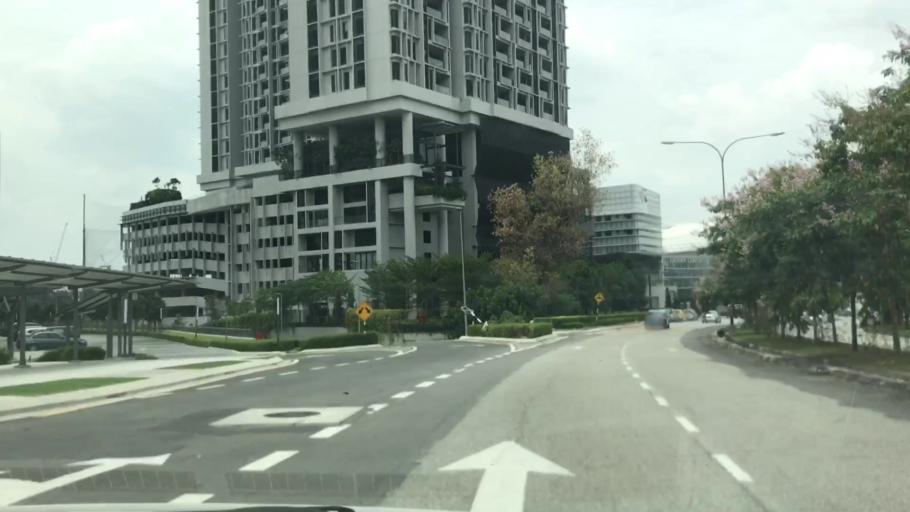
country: MY
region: Selangor
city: Kampong Baharu Balakong
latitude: 3.0521
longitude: 101.6786
